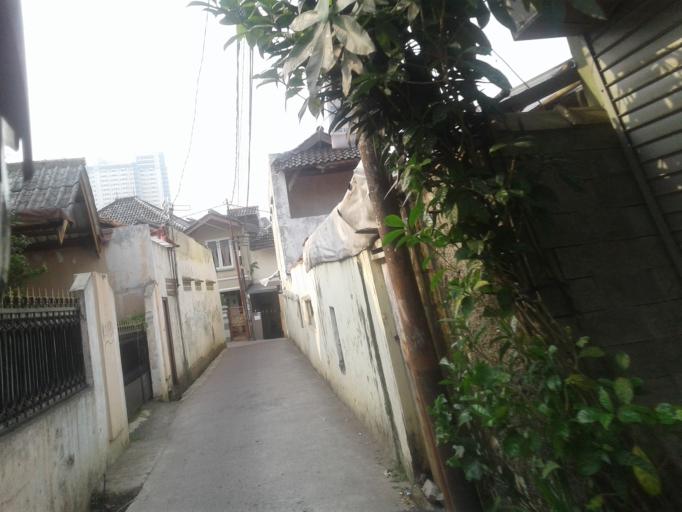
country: ID
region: West Java
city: Depok
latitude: -6.3706
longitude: 106.8352
